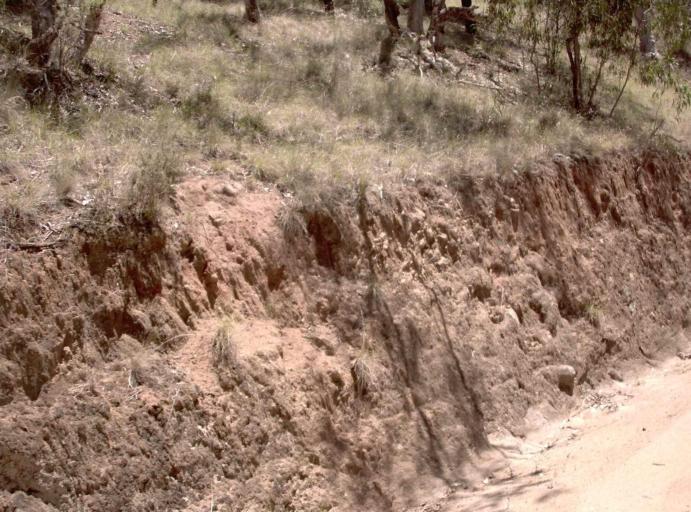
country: AU
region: New South Wales
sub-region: Snowy River
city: Jindabyne
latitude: -36.9343
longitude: 148.3643
